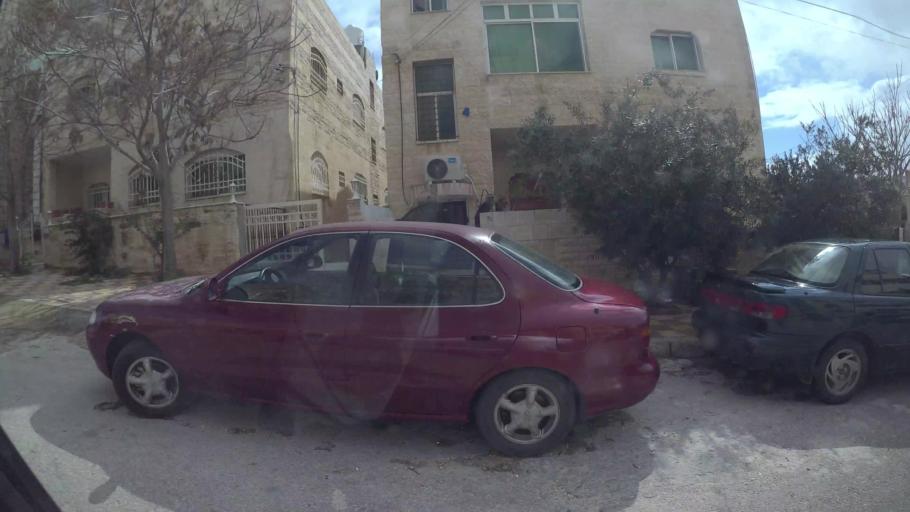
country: JO
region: Amman
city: Al Jubayhah
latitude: 32.0639
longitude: 35.8803
